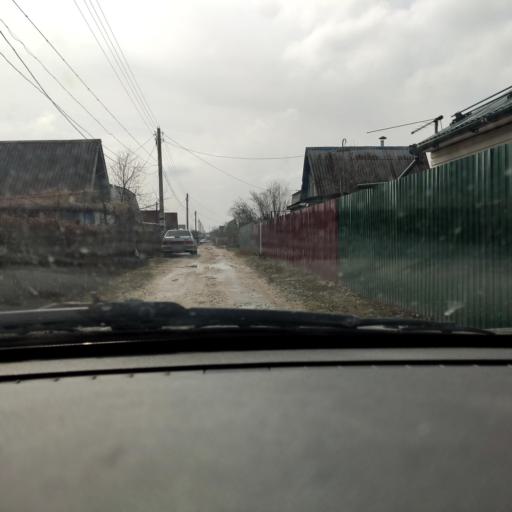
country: RU
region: Samara
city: Tol'yatti
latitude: 53.5866
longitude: 49.2916
